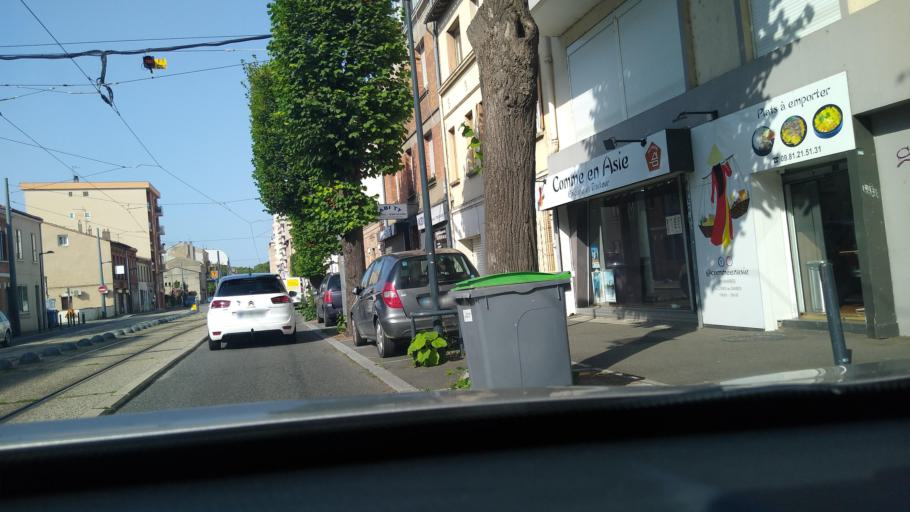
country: FR
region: Midi-Pyrenees
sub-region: Departement de la Haute-Garonne
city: Toulouse
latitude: 43.5885
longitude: 1.4312
